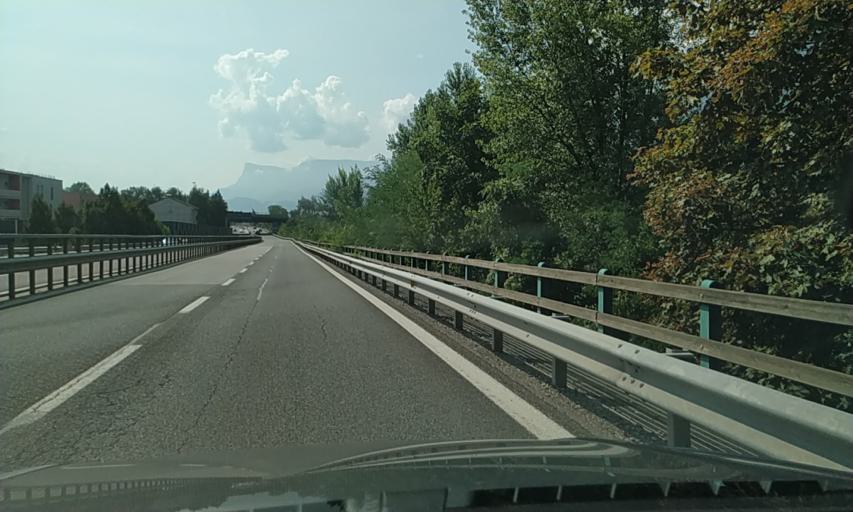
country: IT
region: Trentino-Alto Adige
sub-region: Bolzano
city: Marlengo
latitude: 46.6615
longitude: 11.1445
